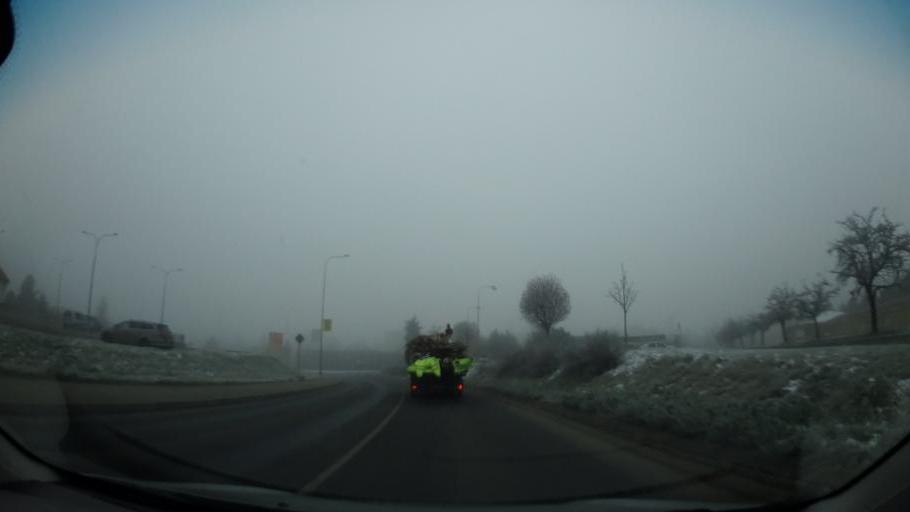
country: CZ
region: Vysocina
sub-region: Okres Trebic
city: Trebic
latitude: 49.2237
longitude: 15.8944
